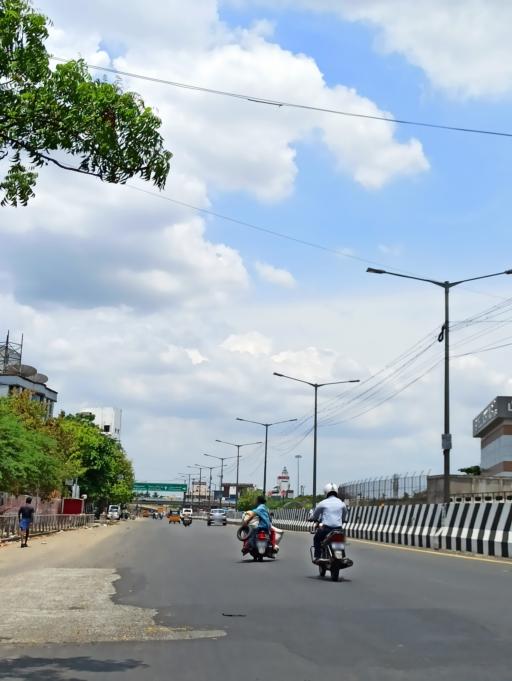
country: IN
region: Tamil Nadu
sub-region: Thiruvallur
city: Ambattur
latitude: 13.0805
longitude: 80.1987
